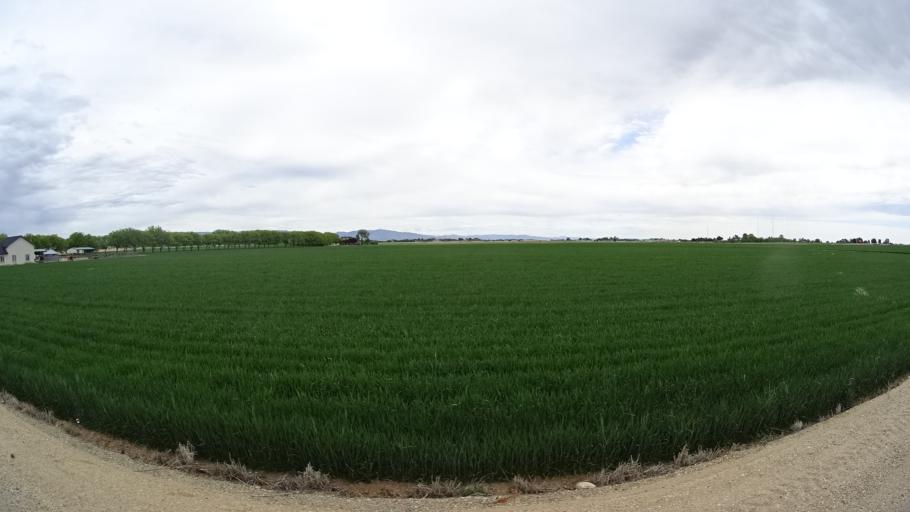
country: US
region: Idaho
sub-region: Ada County
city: Meridian
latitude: 43.5693
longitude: -116.4137
